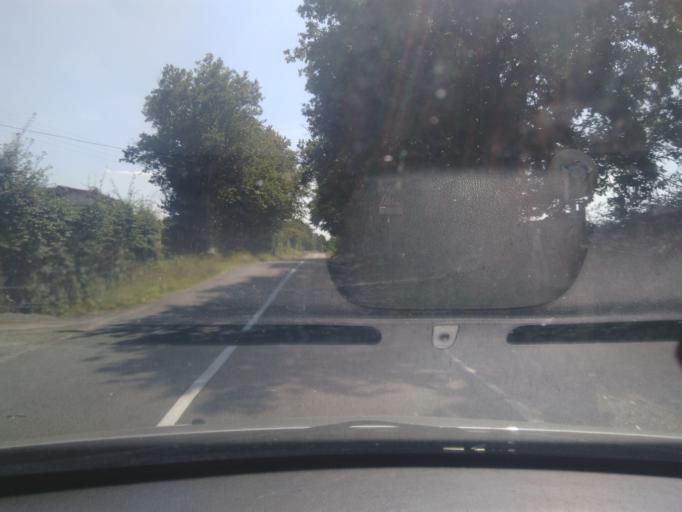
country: FR
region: Pays de la Loire
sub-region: Departement de la Vendee
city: La Ferriere
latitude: 46.6823
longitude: -1.3489
